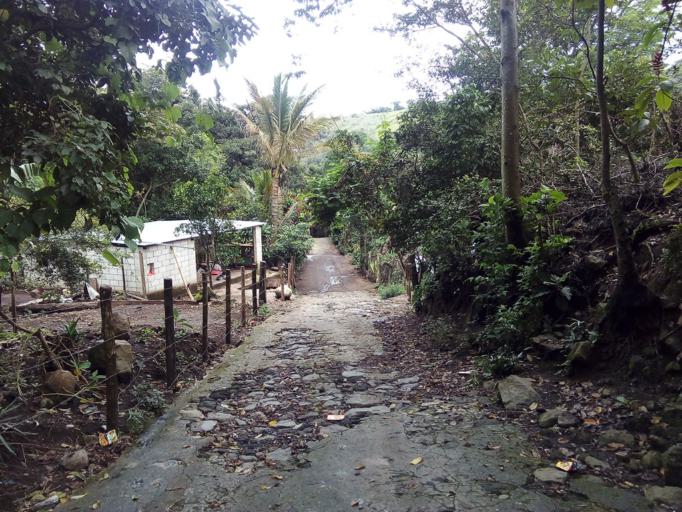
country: GT
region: Escuintla
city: San Vicente Pacaya
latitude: 14.3295
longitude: -90.6046
